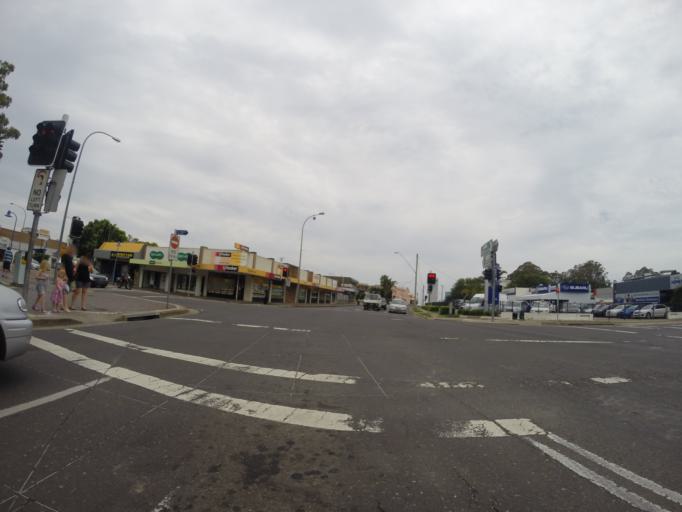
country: AU
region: New South Wales
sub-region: Eurobodalla
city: Batemans Bay
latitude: -35.7084
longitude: 150.1774
